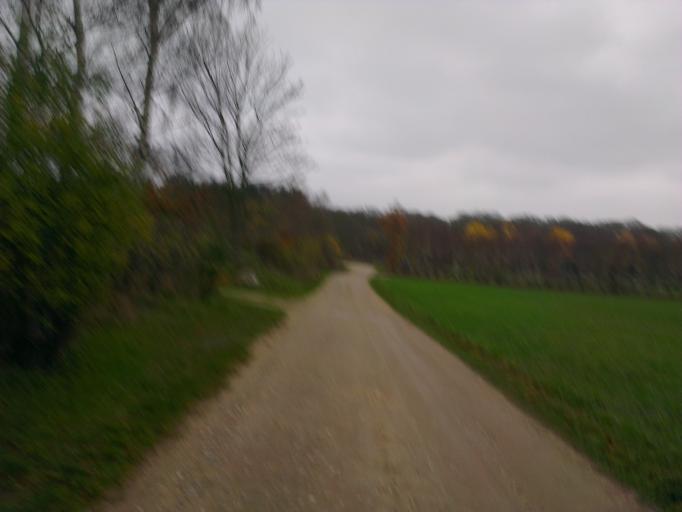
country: DK
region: Capital Region
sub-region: Frederikssund Kommune
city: Jaegerspris
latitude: 55.8489
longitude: 12.0077
